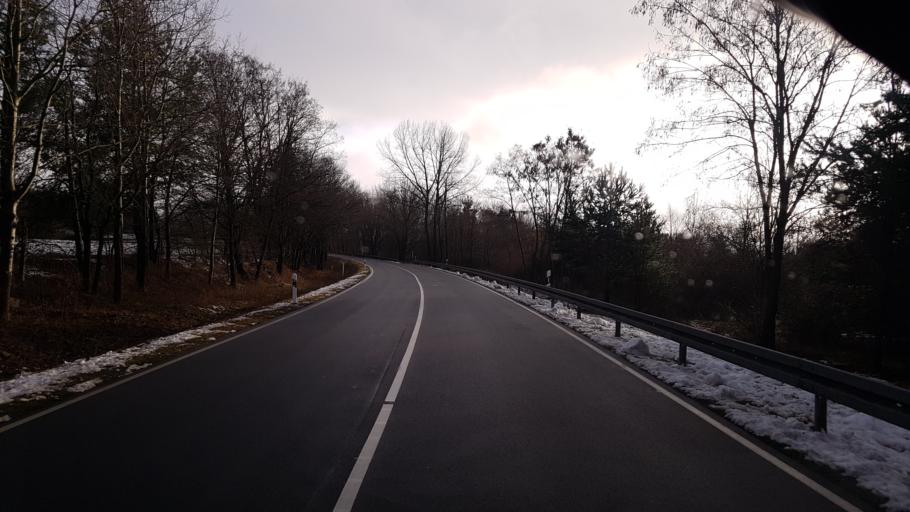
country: DE
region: Brandenburg
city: Heinersbruck
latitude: 51.8229
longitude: 14.5839
